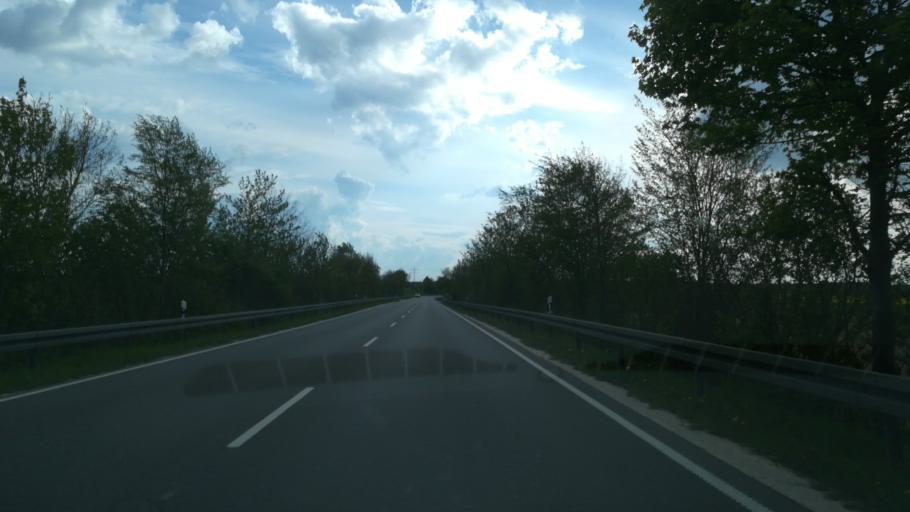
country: DE
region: Baden-Wuerttemberg
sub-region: Tuebingen Region
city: Messkirch
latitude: 48.0003
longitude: 9.0985
